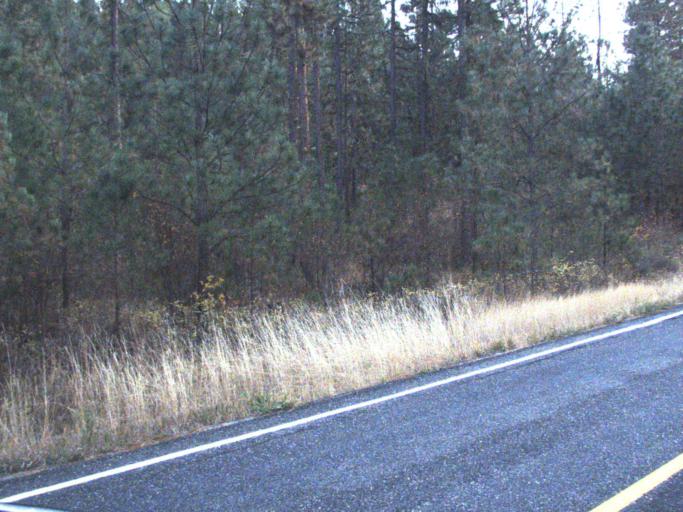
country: US
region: Washington
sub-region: Stevens County
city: Kettle Falls
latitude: 48.2105
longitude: -118.1785
